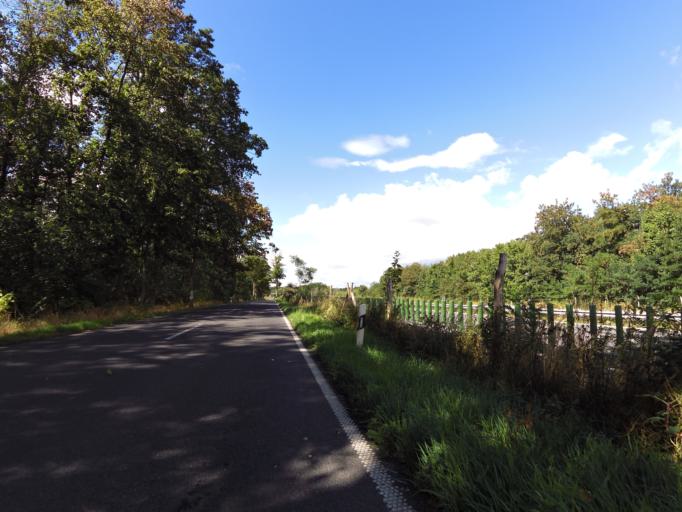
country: DE
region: Brandenburg
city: Grossbeeren
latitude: 52.3719
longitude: 13.3548
